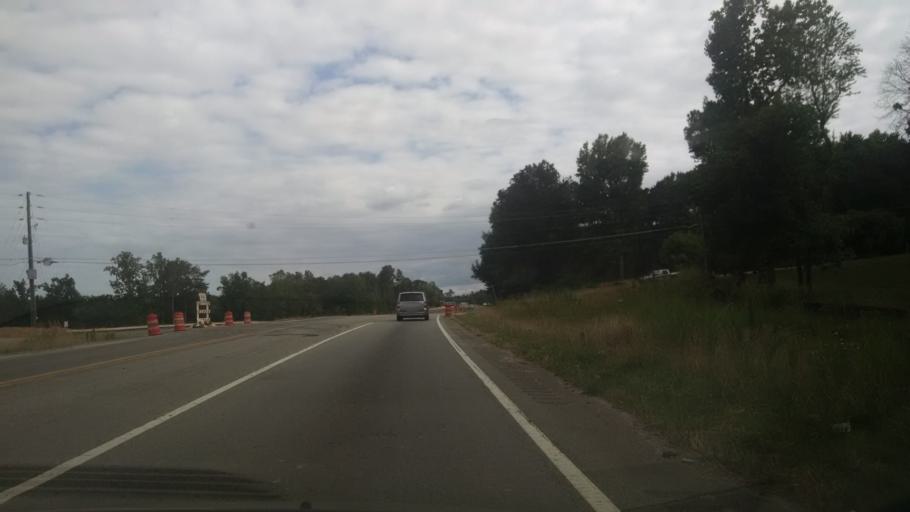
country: US
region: Georgia
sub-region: Forsyth County
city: Cumming
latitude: 34.1490
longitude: -84.1048
